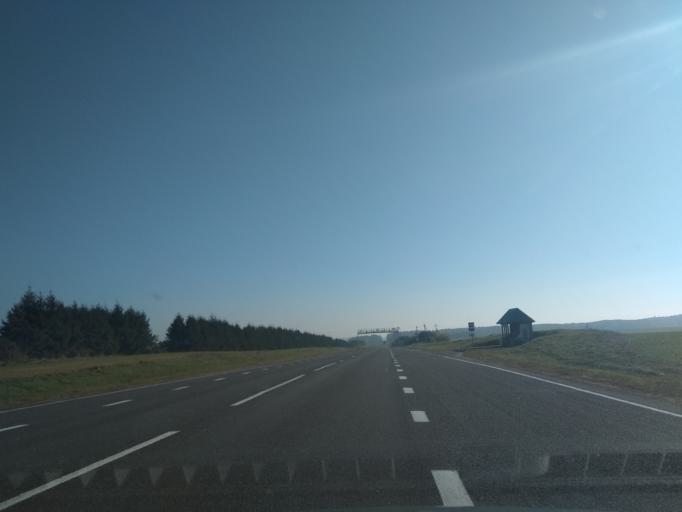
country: BY
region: Grodnenskaya
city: Zel'va
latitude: 53.1351
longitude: 24.9729
